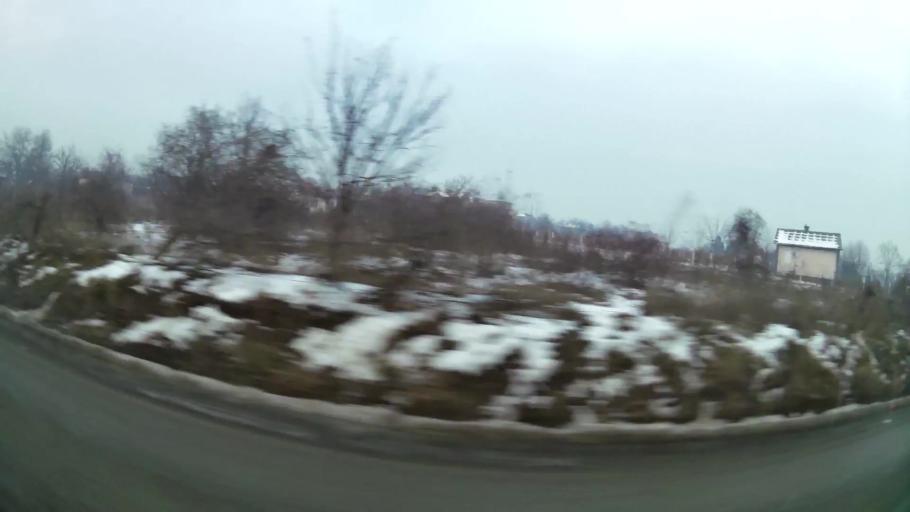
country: MK
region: Suto Orizari
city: Suto Orizare
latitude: 42.0310
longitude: 21.4071
